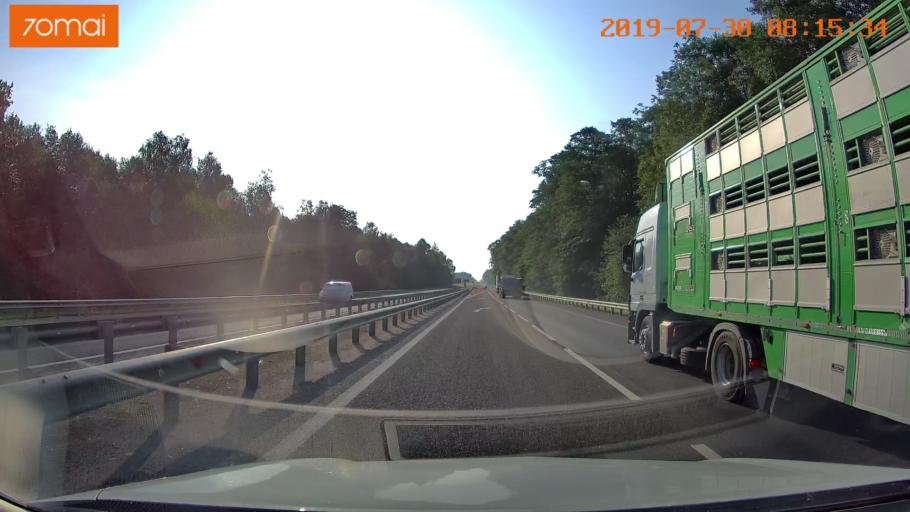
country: RU
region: Kaliningrad
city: Zheleznodorozhnyy
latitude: 54.6435
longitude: 21.3885
